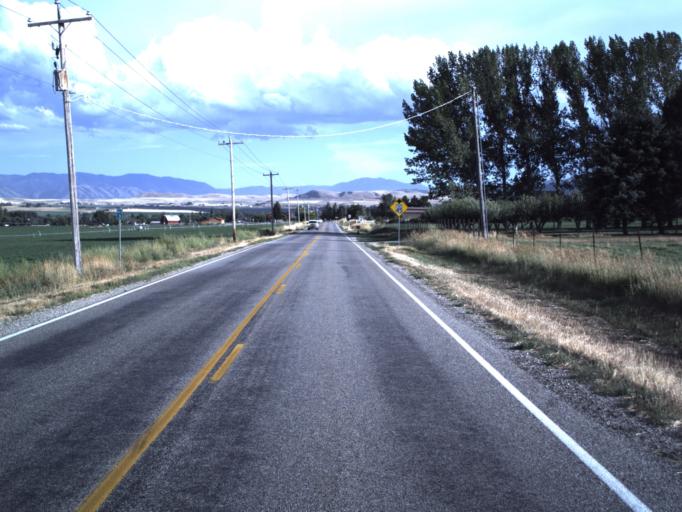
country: US
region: Utah
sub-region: Cache County
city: Wellsville
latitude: 41.6560
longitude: -111.9435
